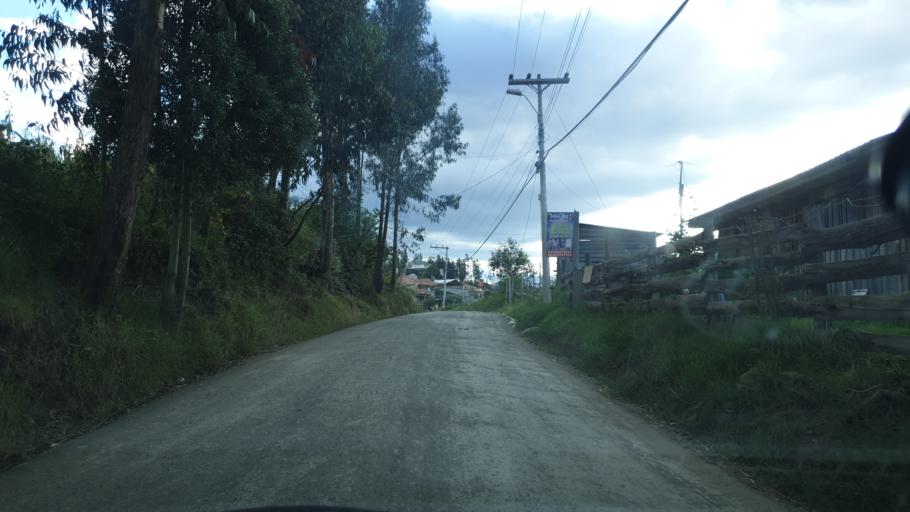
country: EC
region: Azuay
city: Cuenca
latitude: -2.9246
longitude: -78.9688
